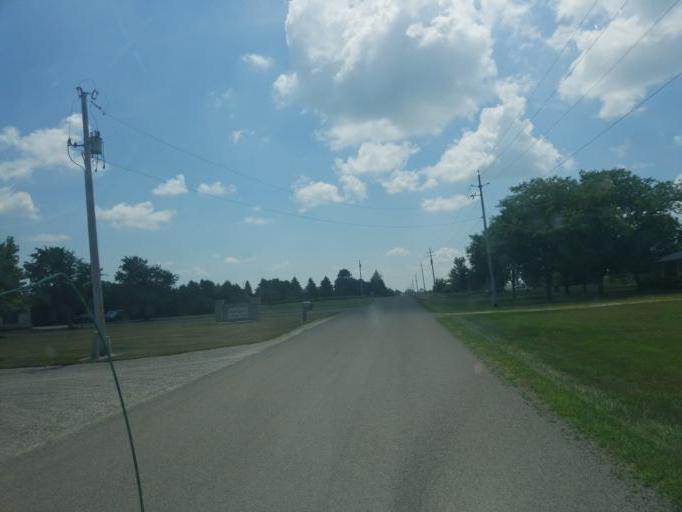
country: US
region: Ohio
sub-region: Mercer County
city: Celina
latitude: 40.5747
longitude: -84.4939
